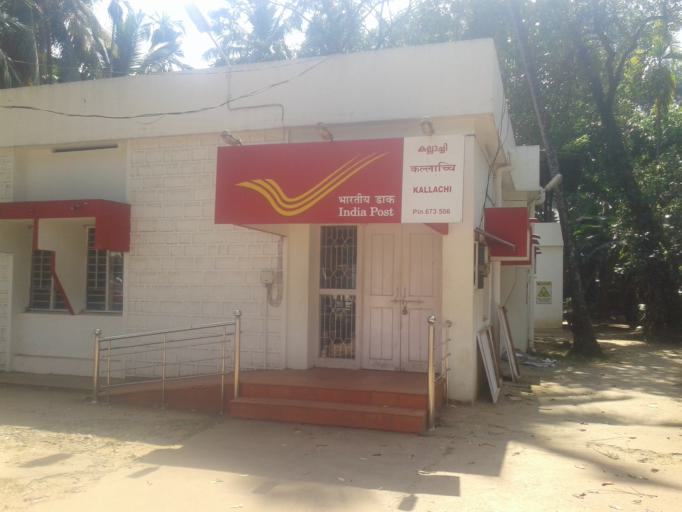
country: IN
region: Kerala
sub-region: Kozhikode
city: Nadapuram
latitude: 11.6900
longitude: 75.6646
